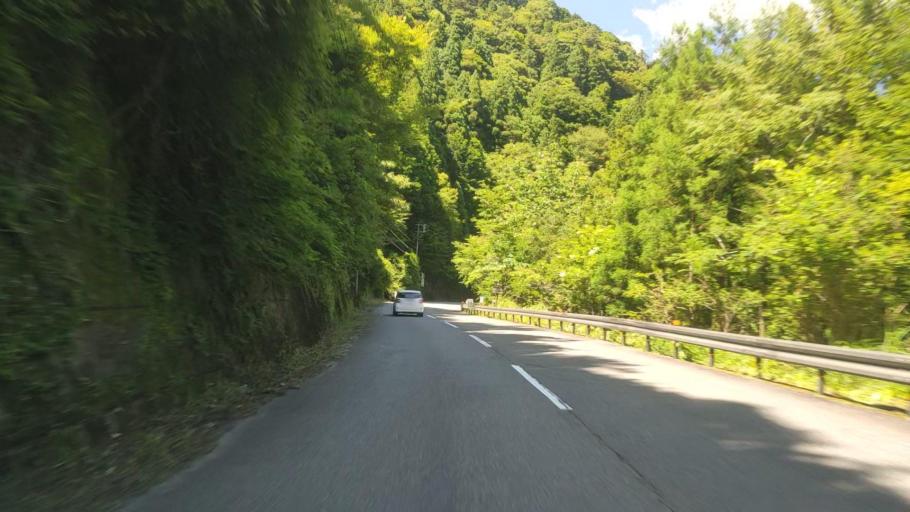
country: JP
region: Mie
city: Owase
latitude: 34.1734
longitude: 136.0023
